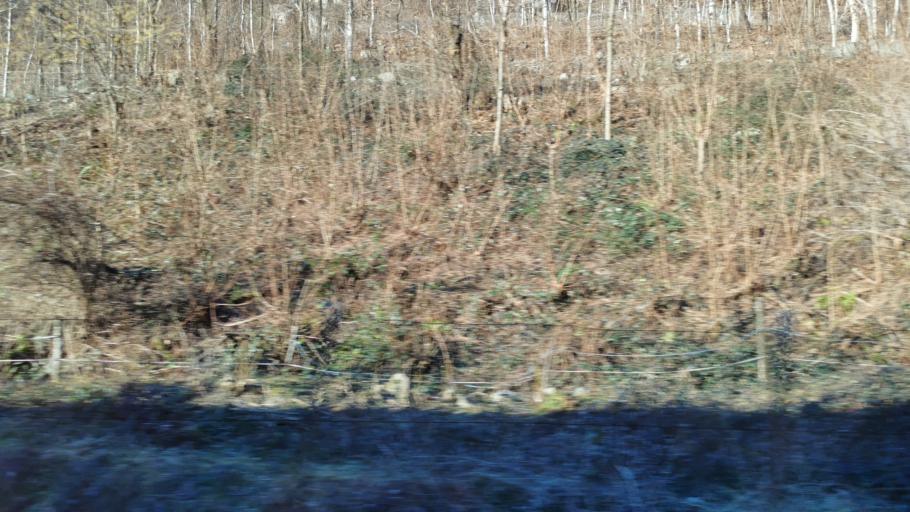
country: CH
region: Ticino
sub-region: Blenio District
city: Cancori
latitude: 46.4175
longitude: 8.8604
